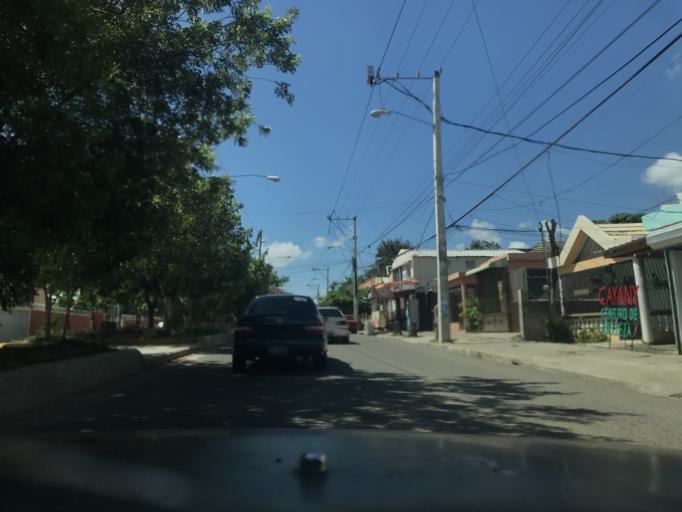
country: DO
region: Santiago
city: Santiago de los Caballeros
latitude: 19.4472
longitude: -70.7423
